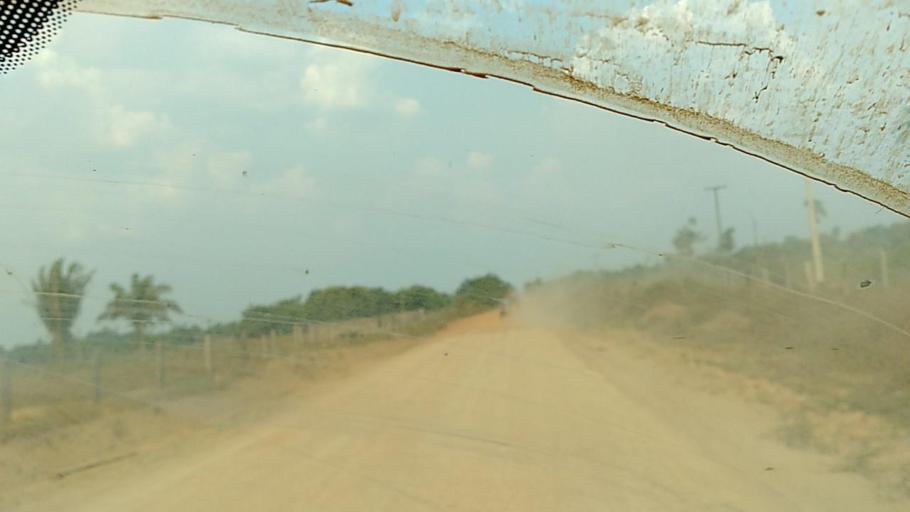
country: BR
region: Rondonia
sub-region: Porto Velho
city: Porto Velho
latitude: -8.6828
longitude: -63.2331
